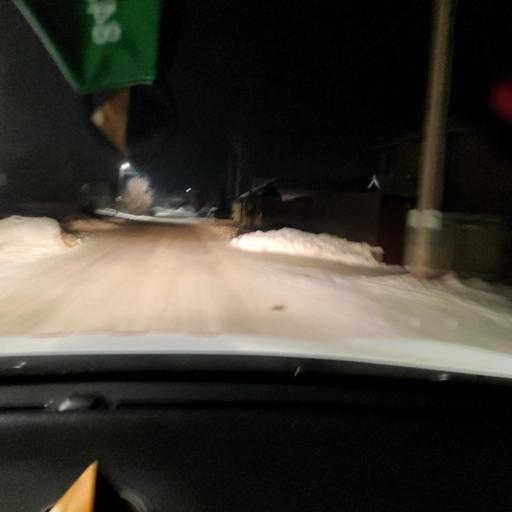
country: RU
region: Tatarstan
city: Stolbishchi
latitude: 55.6519
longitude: 49.2102
